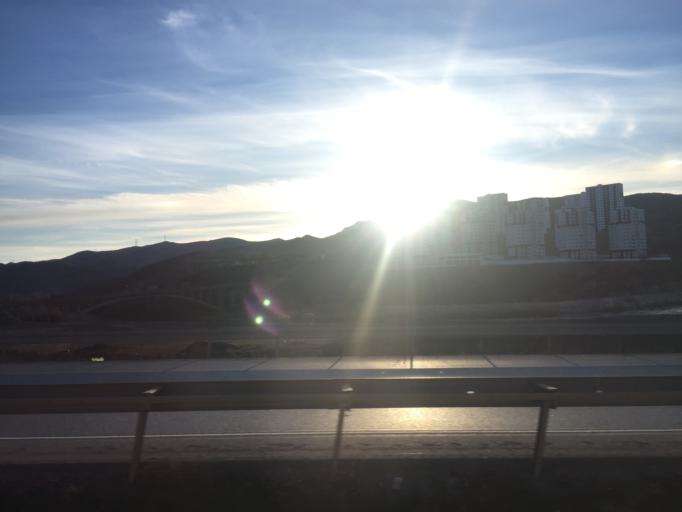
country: TR
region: Kirikkale
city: Yahsihan
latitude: 39.9251
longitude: 33.4301
